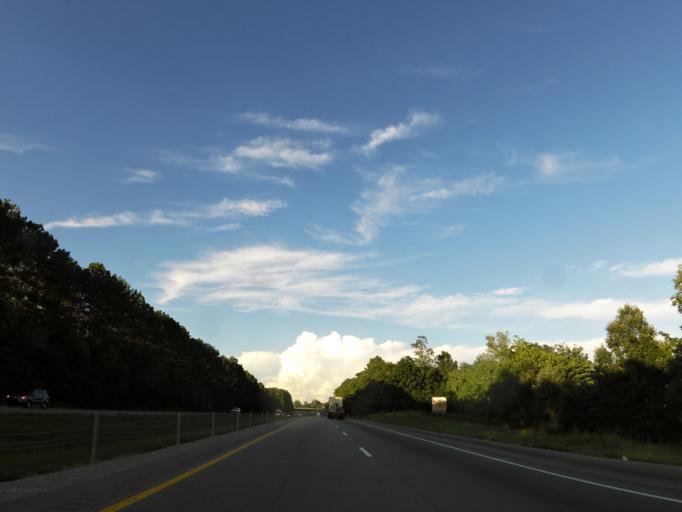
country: US
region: Tennessee
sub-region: Putnam County
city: Baxter
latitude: 36.1059
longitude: -85.6963
